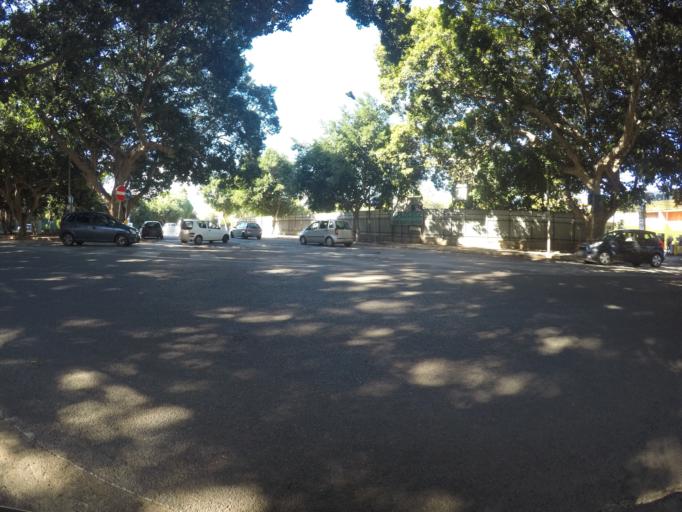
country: IT
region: Sicily
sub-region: Palermo
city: Palermo
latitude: 38.1906
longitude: 13.3329
